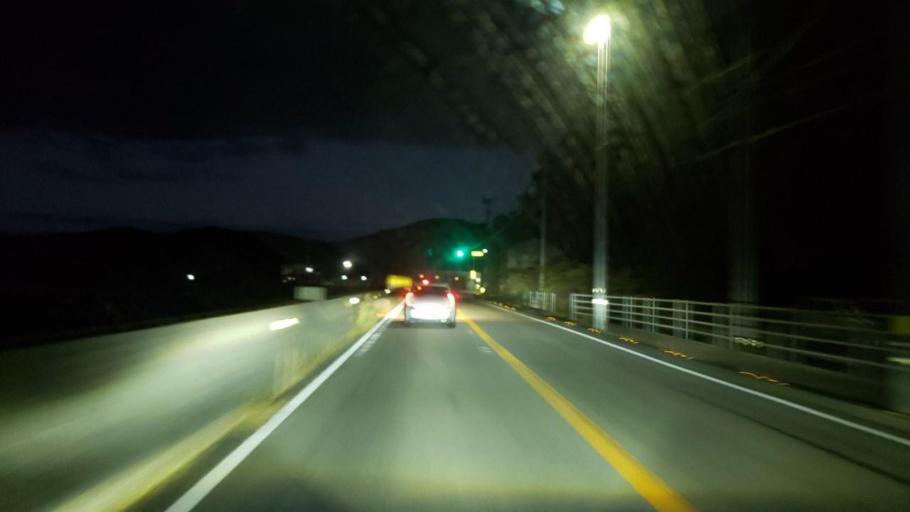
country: JP
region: Tokushima
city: Narutocho-mitsuishi
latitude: 34.2219
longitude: 134.5571
